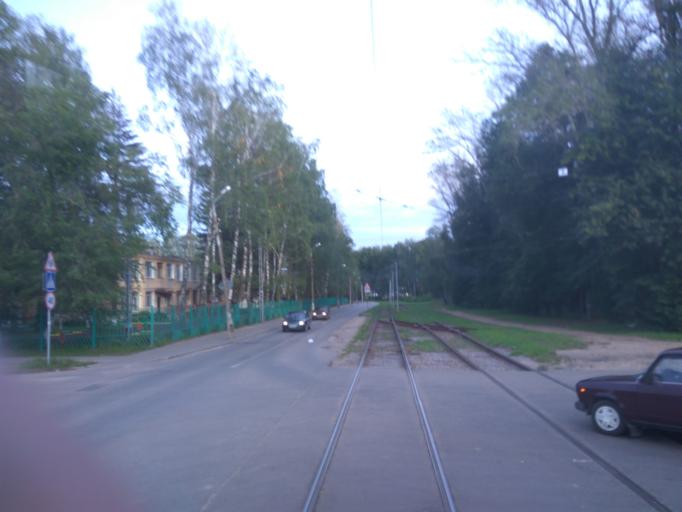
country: RU
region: Moskovskaya
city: Kolomna
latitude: 55.0744
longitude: 38.7844
